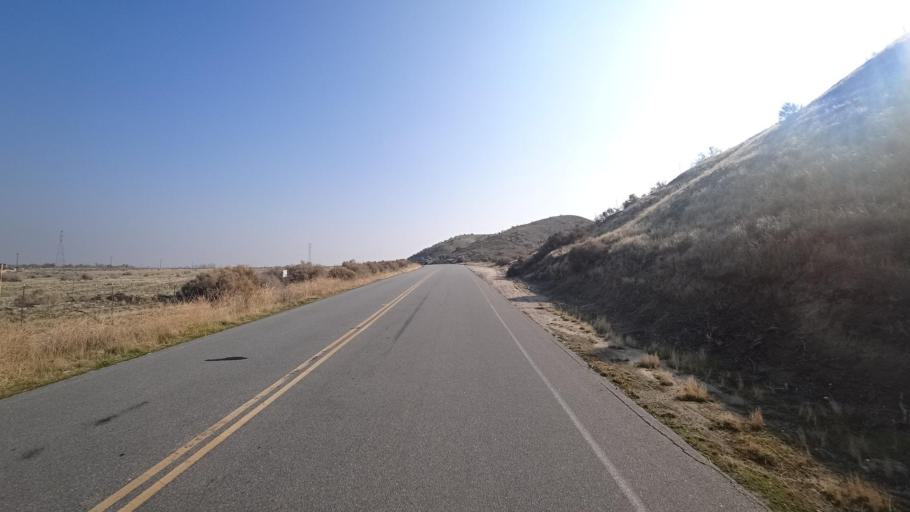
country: US
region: California
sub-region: Kern County
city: Buttonwillow
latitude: 35.2892
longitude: -119.3411
